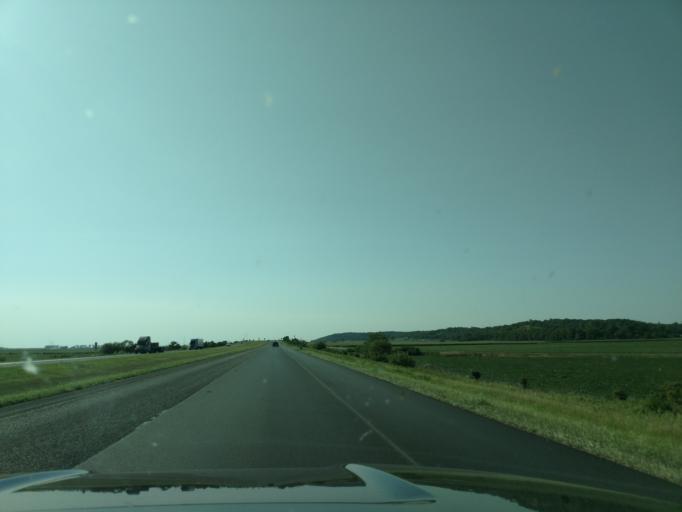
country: US
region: Missouri
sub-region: Atchison County
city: Rock Port
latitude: 40.2478
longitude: -95.4340
